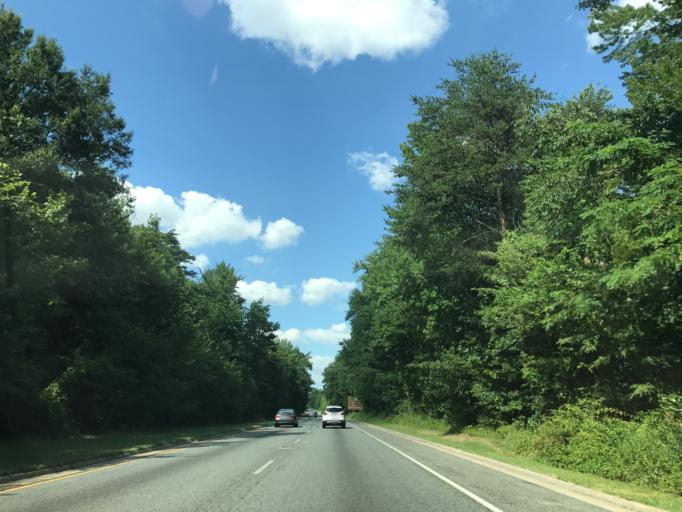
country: US
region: Maryland
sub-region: Anne Arundel County
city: Jessup
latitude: 39.1272
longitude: -76.7629
